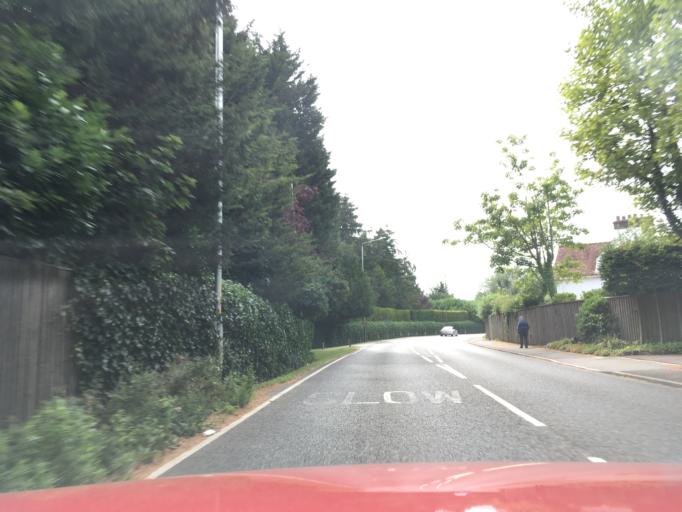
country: GB
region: England
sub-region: Kent
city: Royal Tunbridge Wells
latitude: 51.1312
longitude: 0.2296
